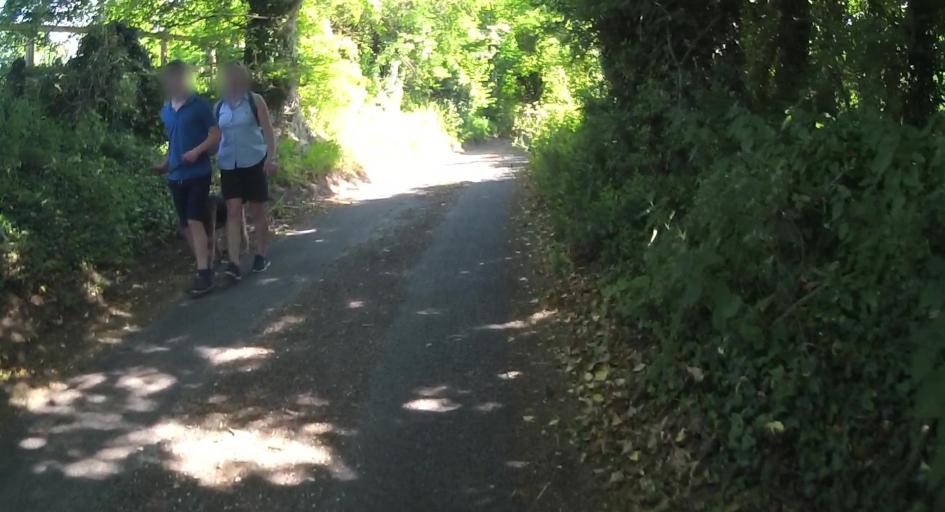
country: GB
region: England
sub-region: Hampshire
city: Old Basing
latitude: 51.2318
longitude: -1.0279
